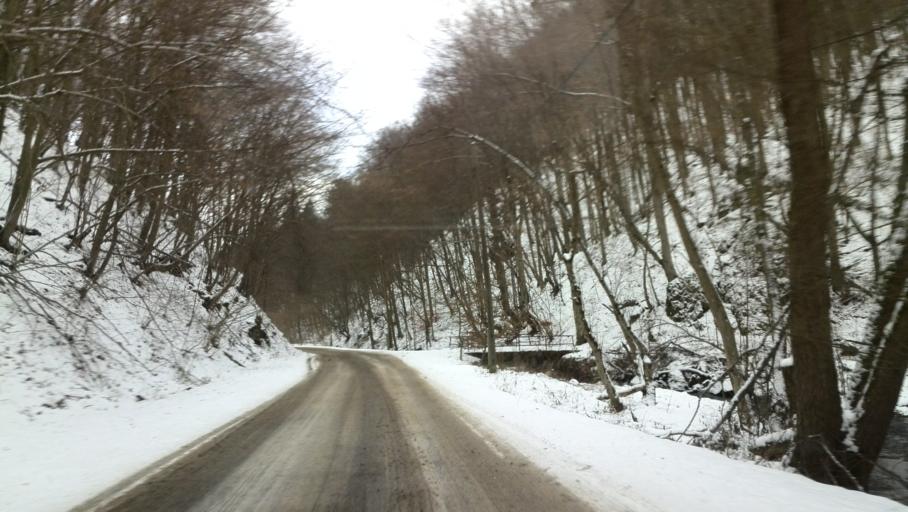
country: SK
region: Kosicky
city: Gelnica
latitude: 48.8194
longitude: 21.0647
